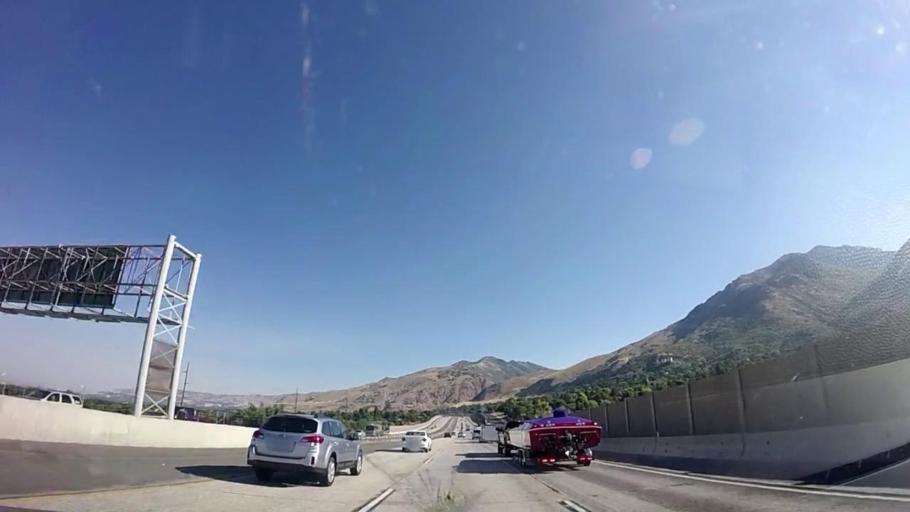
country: US
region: Utah
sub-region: Salt Lake County
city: Mount Olympus
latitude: 40.6894
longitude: -111.7969
